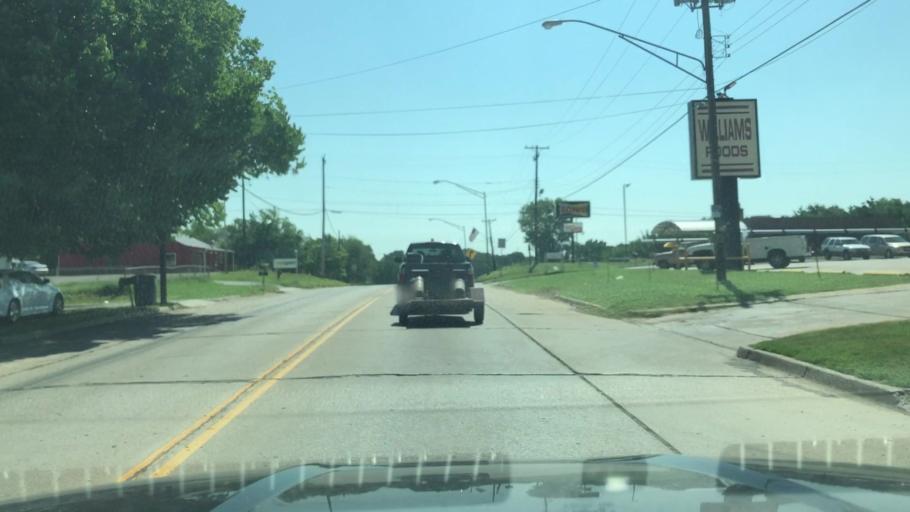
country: US
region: Oklahoma
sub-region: Creek County
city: Drumright
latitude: 35.9885
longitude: -96.5912
